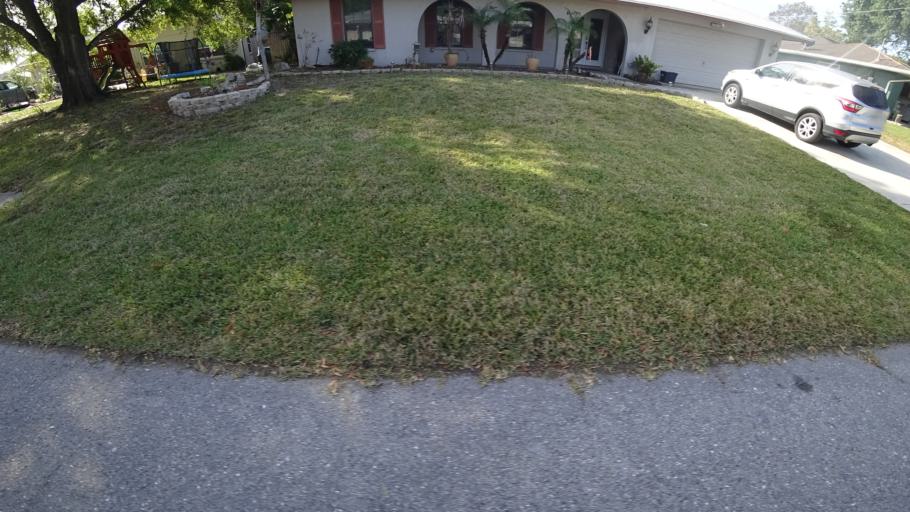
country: US
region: Florida
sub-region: Manatee County
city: Whitfield
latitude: 27.4246
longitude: -82.5490
